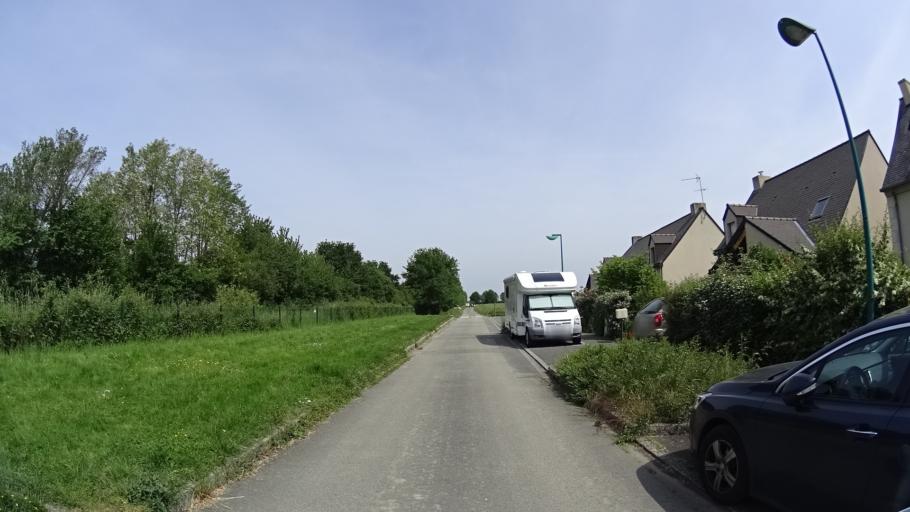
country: FR
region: Brittany
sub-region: Departement d'Ille-et-Vilaine
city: Saint-Armel
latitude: 48.0168
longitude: -1.5948
